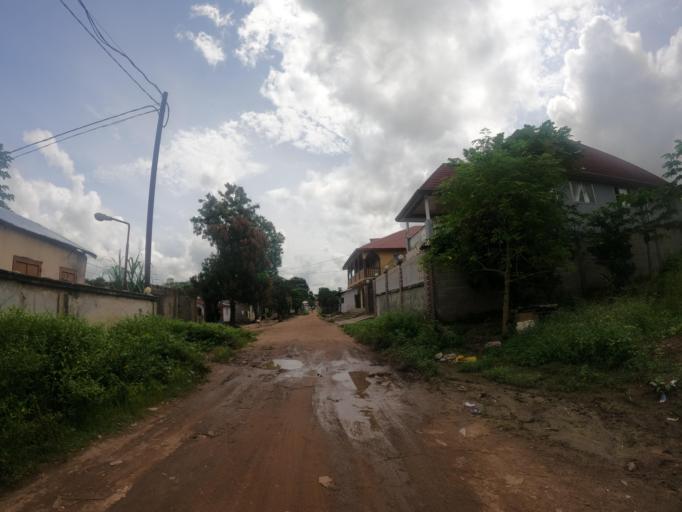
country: SL
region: Northern Province
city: Makeni
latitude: 8.8899
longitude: -12.0657
